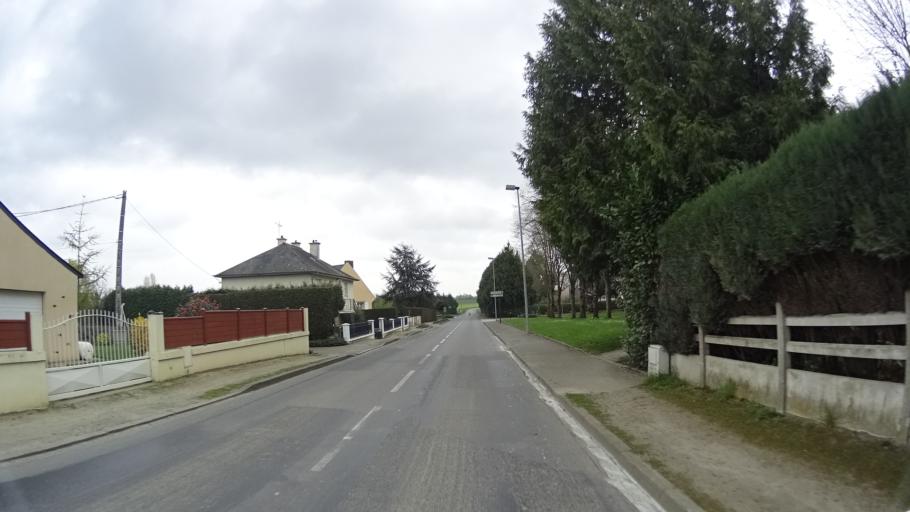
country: FR
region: Brittany
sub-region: Departement d'Ille-et-Vilaine
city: Cintre
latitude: 48.1027
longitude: -1.8688
